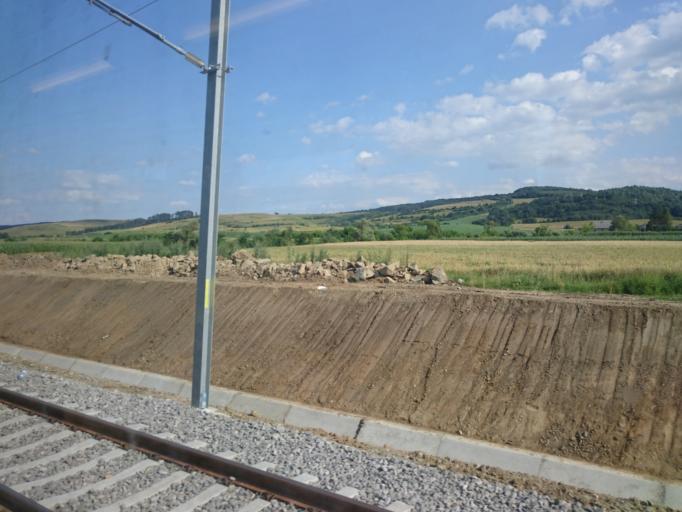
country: RO
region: Sibiu
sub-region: Comuna Laslea
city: Laslea
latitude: 46.2220
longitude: 24.6690
